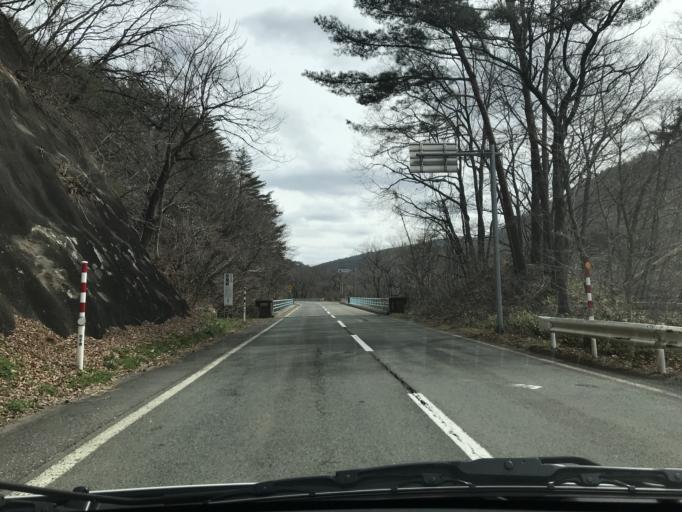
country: JP
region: Iwate
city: Tono
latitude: 39.3042
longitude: 141.3474
